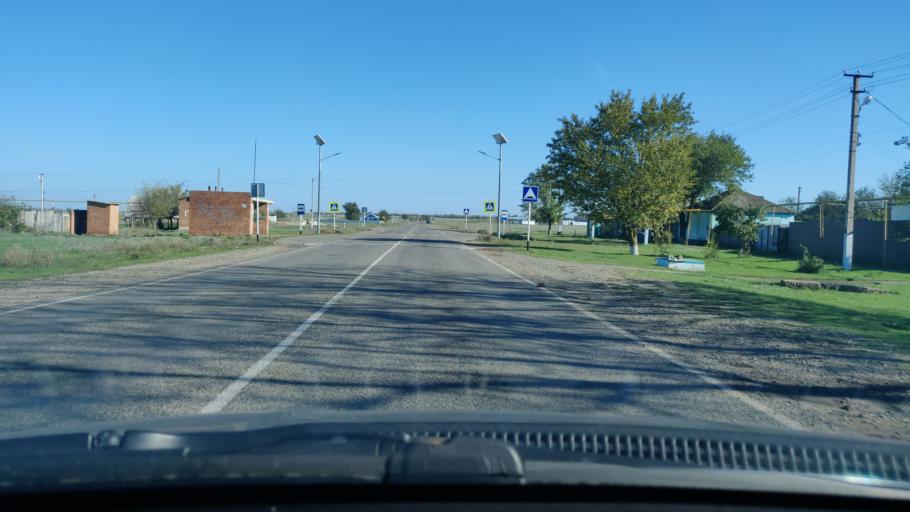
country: RU
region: Stavropol'skiy
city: Letnyaya Stavka
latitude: 45.3749
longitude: 43.6851
